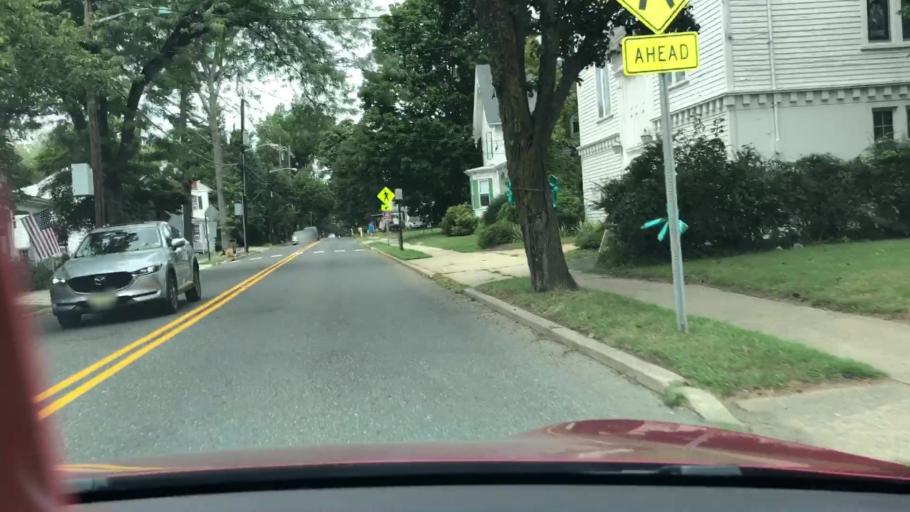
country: US
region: New Jersey
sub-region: Monmouth County
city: Allentown
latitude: 40.1784
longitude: -74.5853
